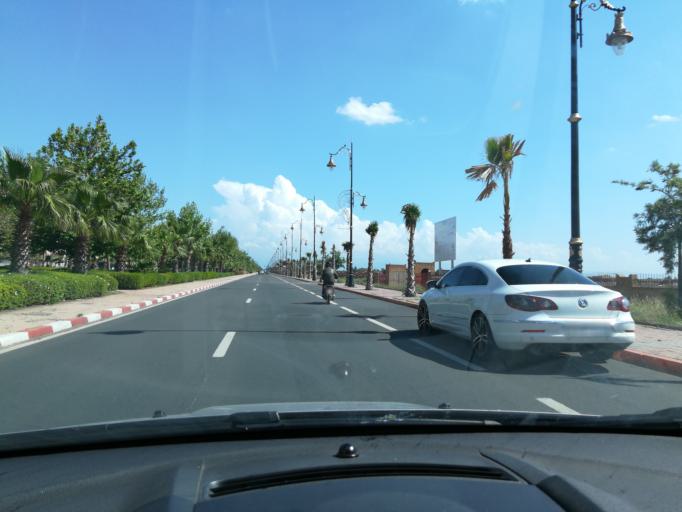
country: MA
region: Marrakech-Tensift-Al Haouz
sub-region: Marrakech
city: Marrakesh
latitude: 31.5996
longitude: -7.9963
